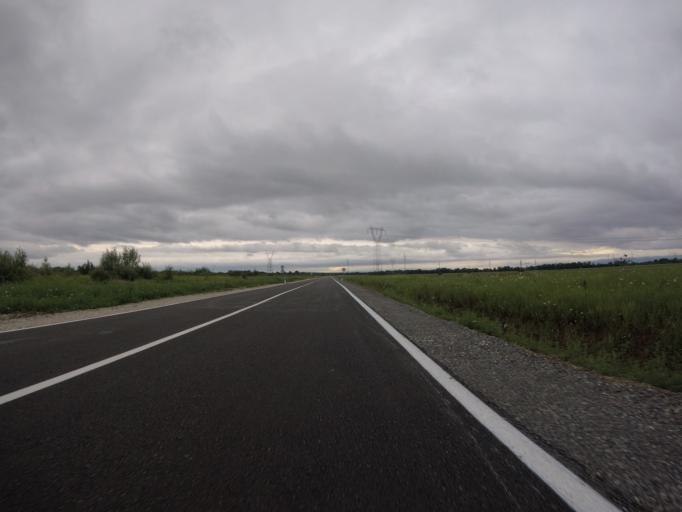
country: HR
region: Zagrebacka
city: Mraclin
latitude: 45.6557
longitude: 16.1136
